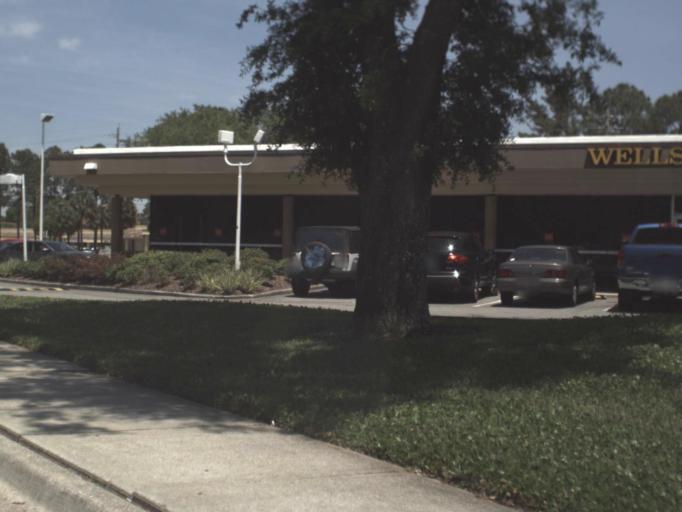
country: US
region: Florida
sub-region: Saint Johns County
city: Fruit Cove
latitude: 30.2202
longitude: -81.5578
